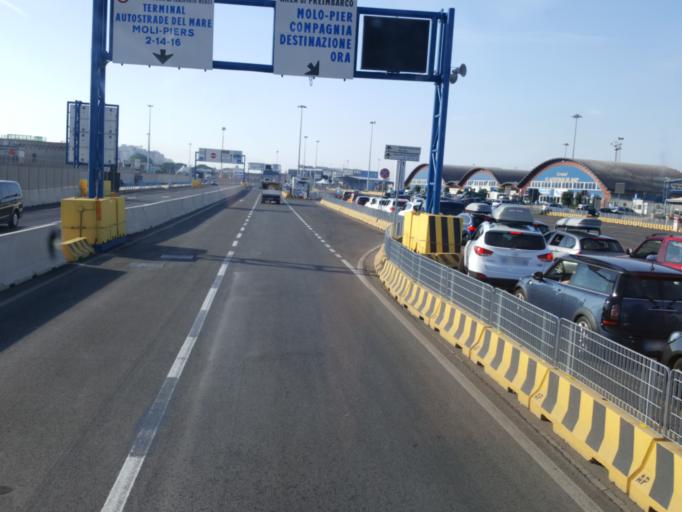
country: IT
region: Latium
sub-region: Citta metropolitana di Roma Capitale
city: Civitavecchia
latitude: 42.1008
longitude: 11.7834
